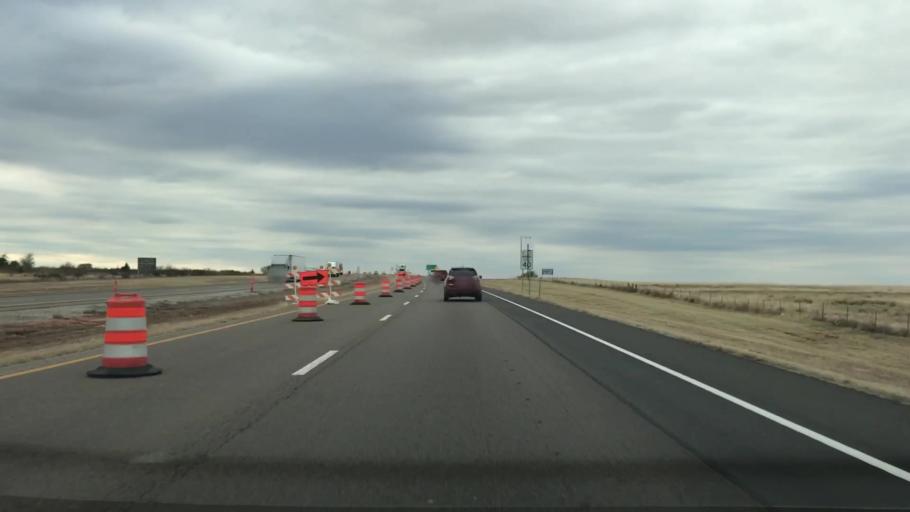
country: US
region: Oklahoma
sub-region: Beckham County
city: Elk City
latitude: 35.4265
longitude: -99.2875
